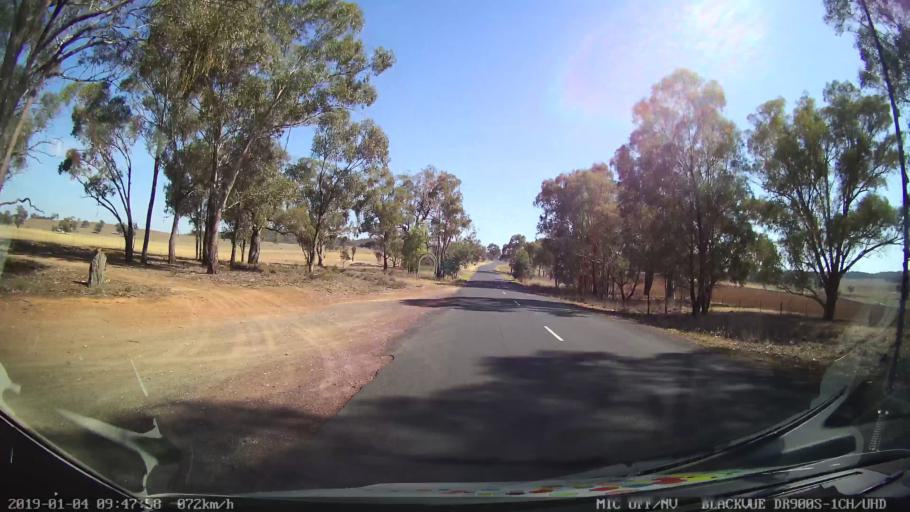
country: AU
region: New South Wales
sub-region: Cabonne
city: Canowindra
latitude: -33.6010
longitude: 148.4320
